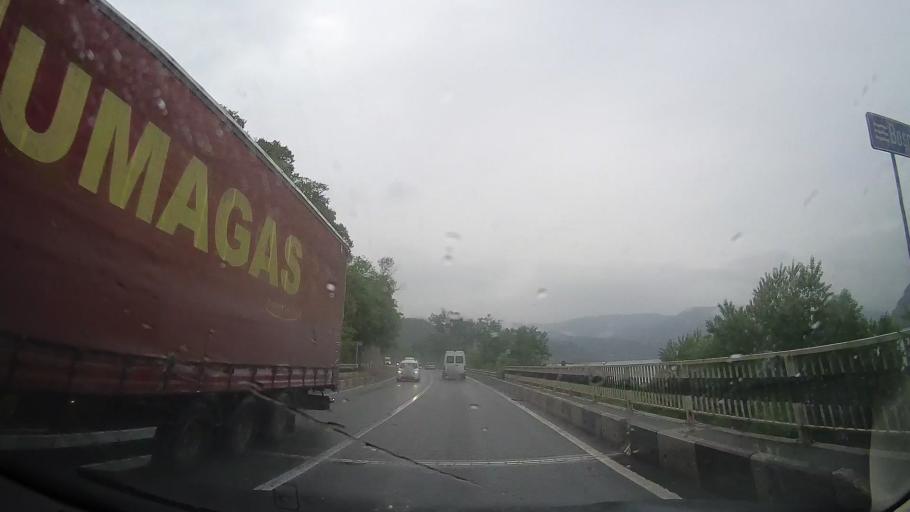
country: RO
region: Mehedinti
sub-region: Comuna Ilovita
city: Ilovita
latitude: 44.7180
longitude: 22.4442
